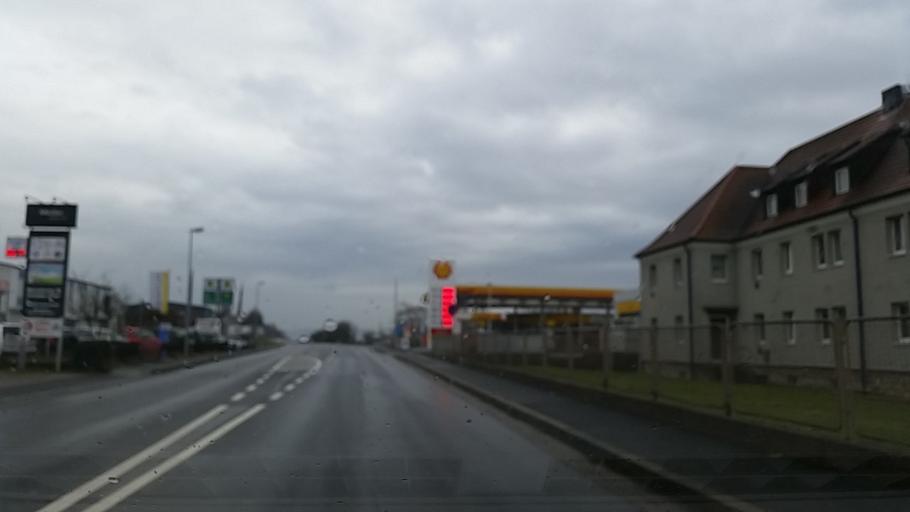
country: DE
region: Bavaria
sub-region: Regierungsbezirk Unterfranken
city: Karlstadt
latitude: 49.9540
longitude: 9.7742
